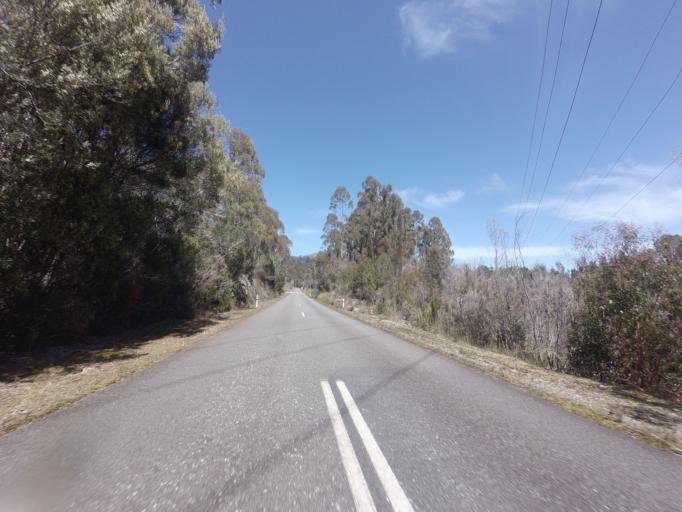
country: AU
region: Tasmania
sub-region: Huon Valley
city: Geeveston
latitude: -42.8324
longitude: 146.2684
